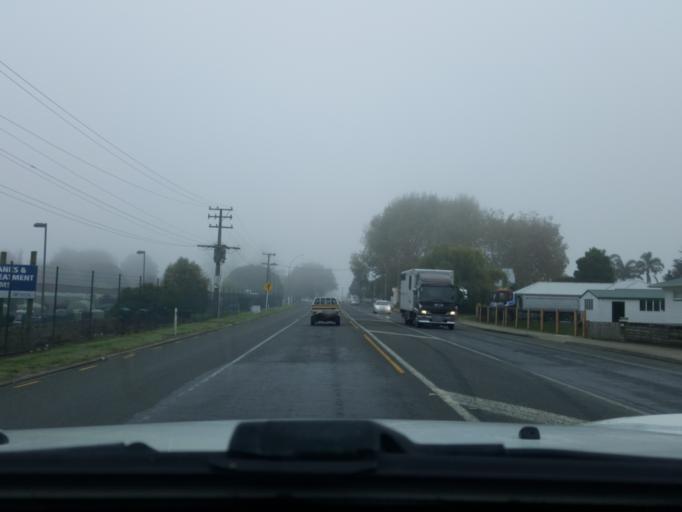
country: NZ
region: Waikato
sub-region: Waikato District
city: Ngaruawahia
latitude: -37.7003
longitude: 175.1975
